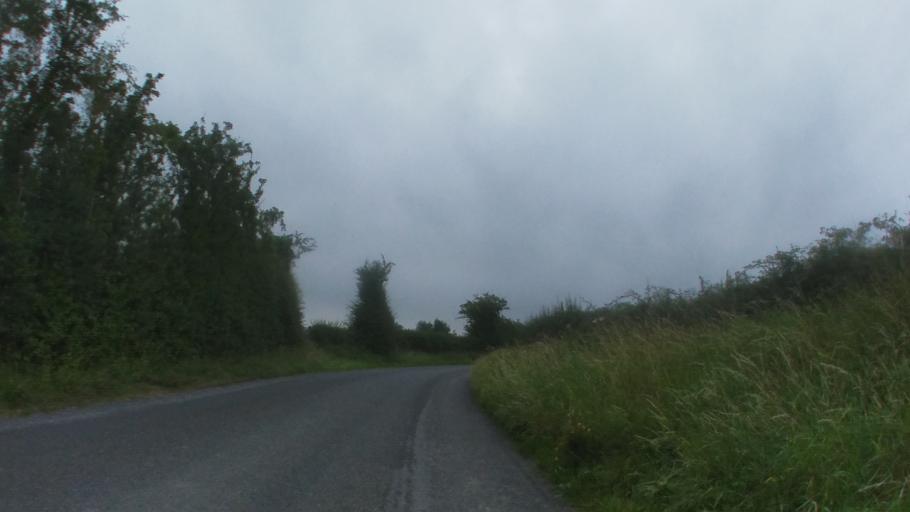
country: IE
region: Leinster
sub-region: Kilkenny
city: Kilkenny
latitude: 52.6986
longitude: -7.1973
